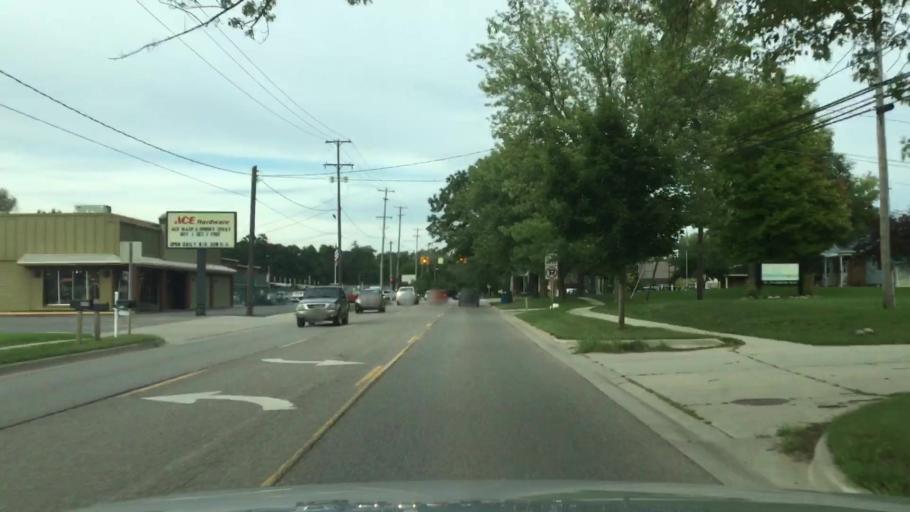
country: US
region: Michigan
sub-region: Genesee County
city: Linden
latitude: 42.8119
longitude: -83.7918
